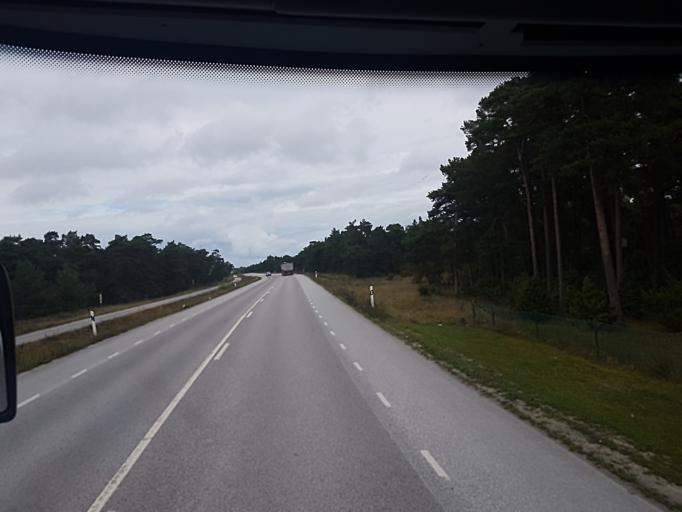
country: SE
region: Gotland
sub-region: Gotland
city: Vibble
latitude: 57.5617
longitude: 18.2036
